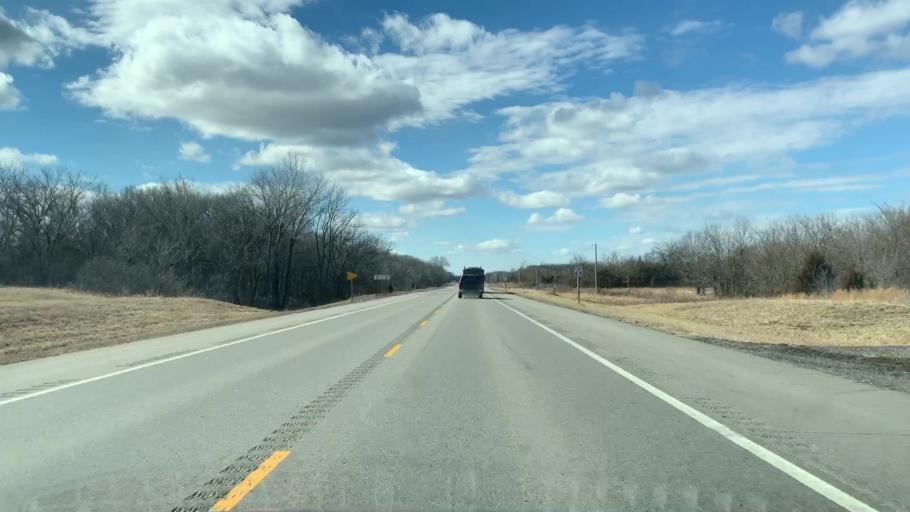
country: US
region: Kansas
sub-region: Cherokee County
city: Columbus
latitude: 37.3400
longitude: -94.9247
